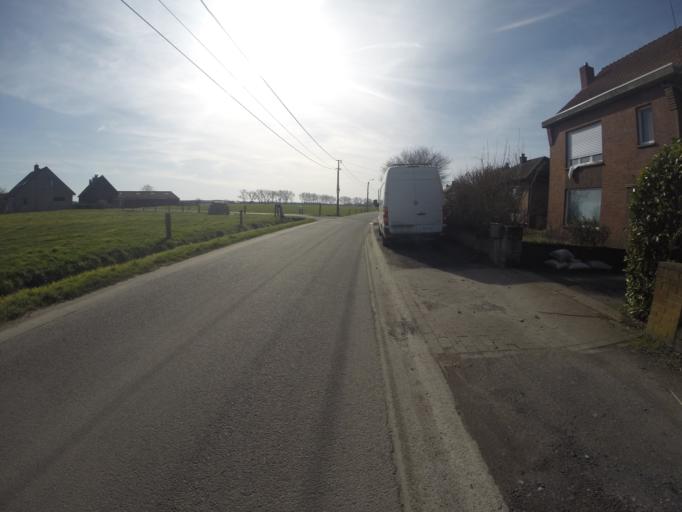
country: BE
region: Flanders
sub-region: Provincie West-Vlaanderen
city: Oostkamp
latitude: 51.1465
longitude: 3.2657
